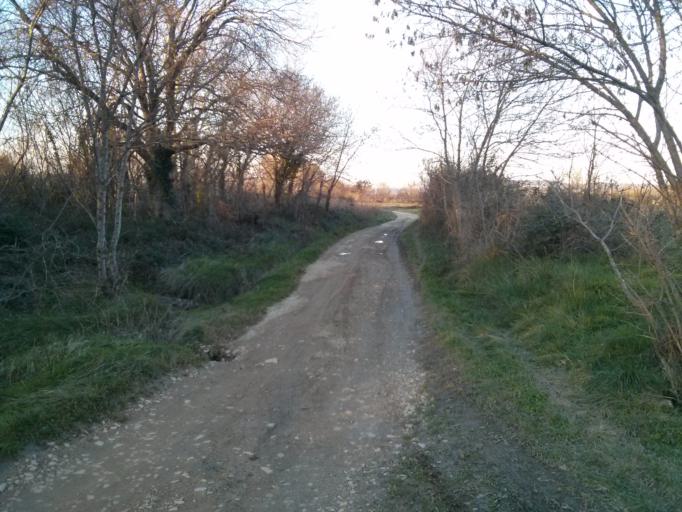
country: FR
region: Languedoc-Roussillon
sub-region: Departement du Gard
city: Vergeze
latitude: 43.7588
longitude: 4.2135
